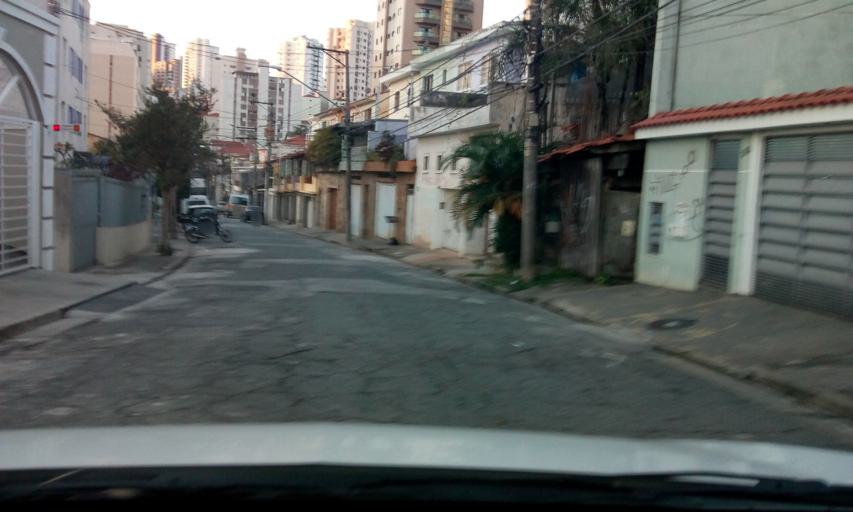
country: BR
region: Sao Paulo
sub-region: Sao Paulo
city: Sao Paulo
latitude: -23.4896
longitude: -46.6163
